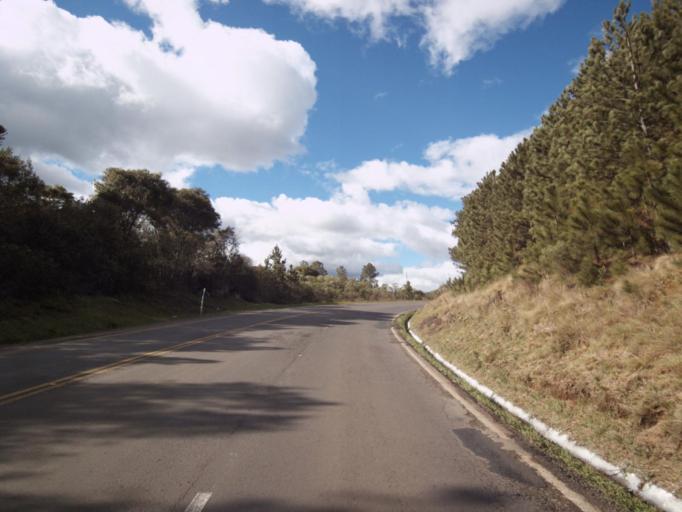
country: BR
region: Santa Catarina
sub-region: Joacaba
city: Joacaba
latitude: -27.0598
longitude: -51.6779
